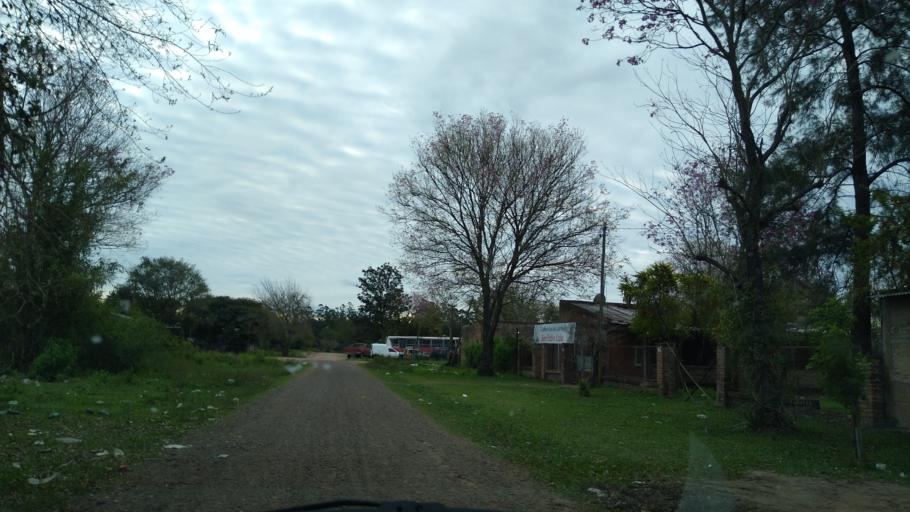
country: AR
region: Chaco
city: Fontana
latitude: -27.4007
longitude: -59.0381
